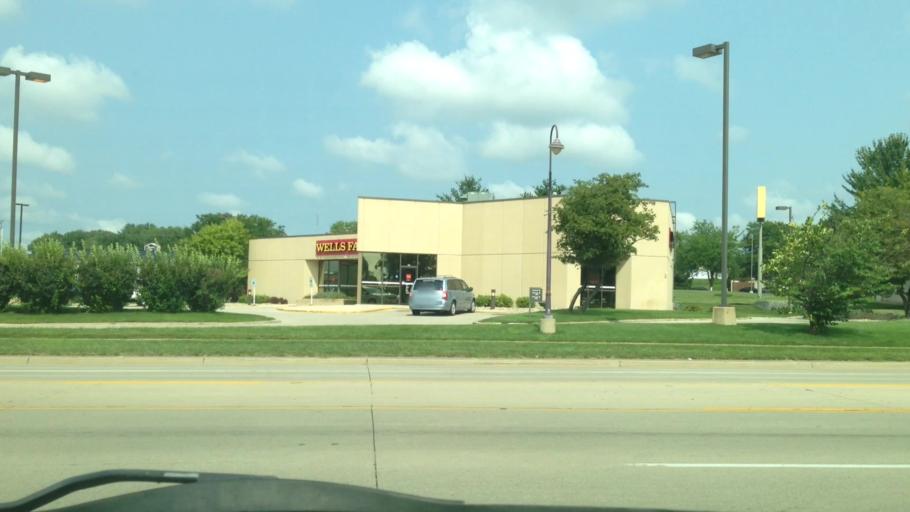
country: US
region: Iowa
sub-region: Linn County
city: Cedar Rapids
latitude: 41.9434
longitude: -91.6741
